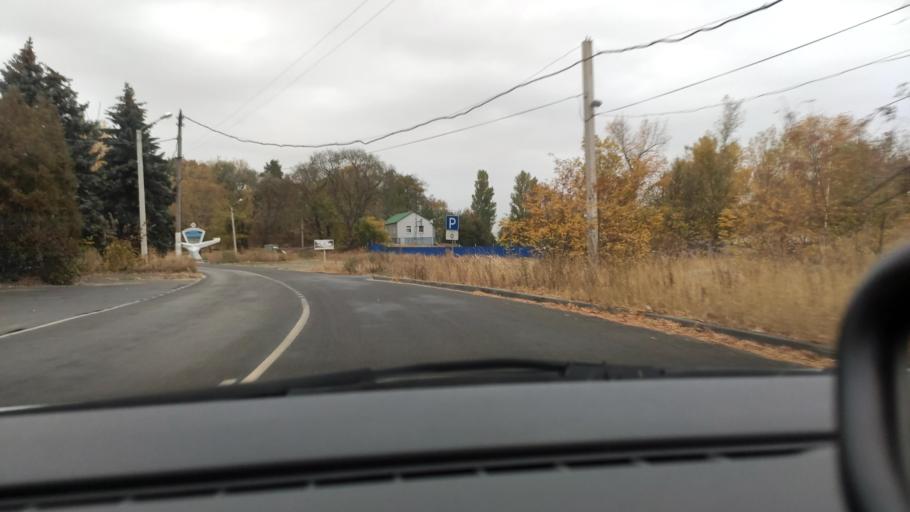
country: RU
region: Voronezj
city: Voronezh
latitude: 51.7252
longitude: 39.2347
